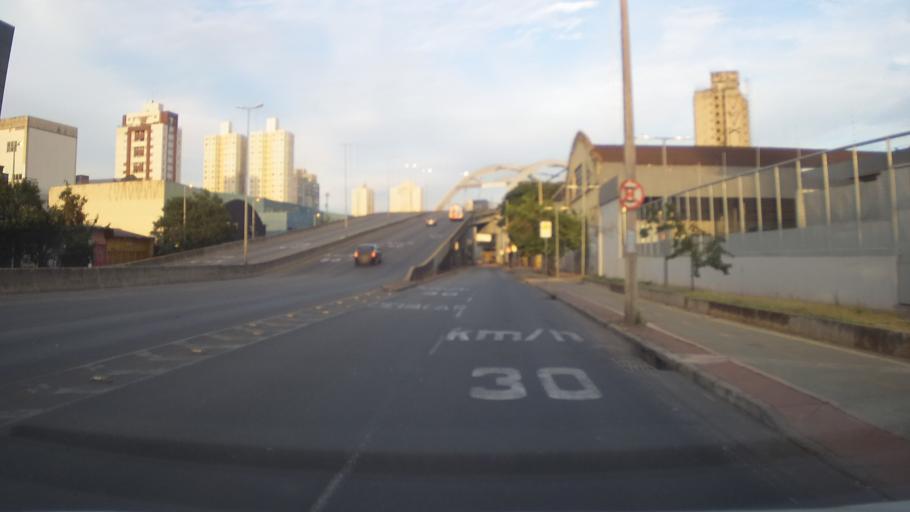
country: BR
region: Minas Gerais
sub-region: Belo Horizonte
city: Belo Horizonte
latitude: -19.9189
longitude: -43.9581
